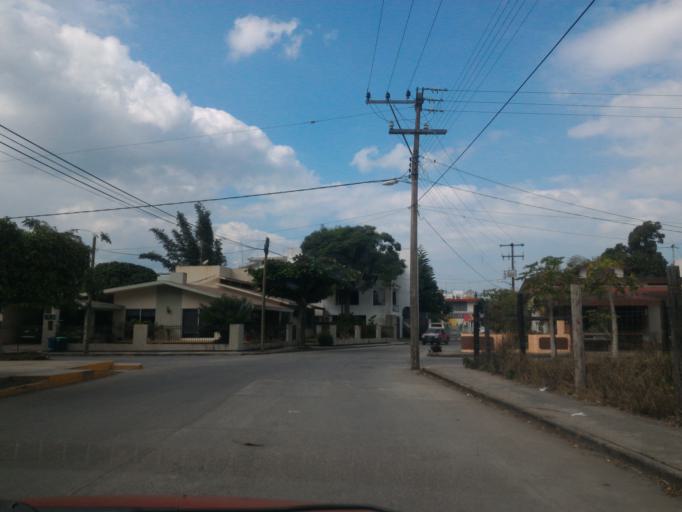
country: MX
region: Veracruz
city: San Rafael
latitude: 20.1840
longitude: -96.8669
